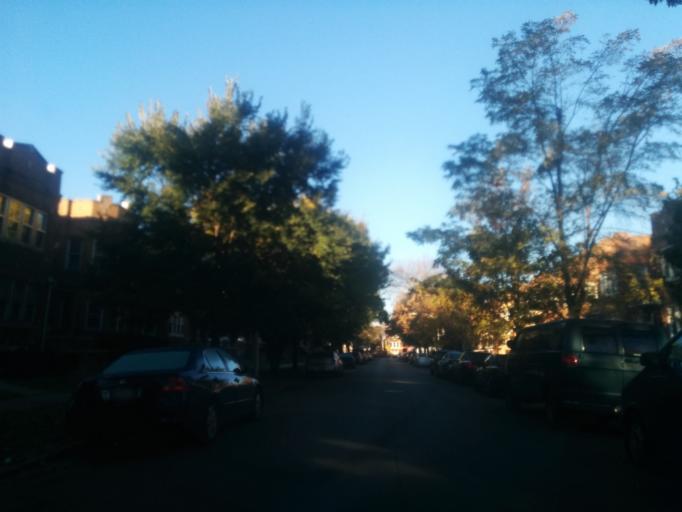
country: US
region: Illinois
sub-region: Cook County
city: Oak Park
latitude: 41.9269
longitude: -87.7592
